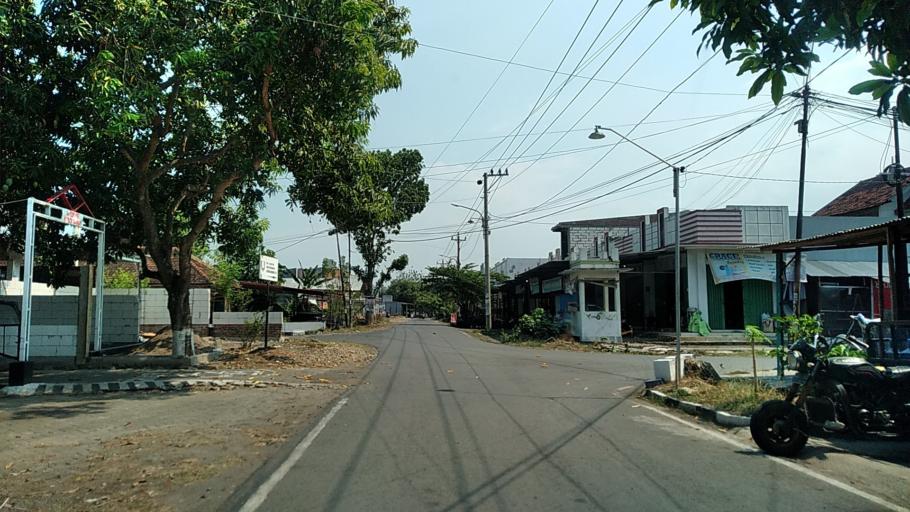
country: ID
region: Central Java
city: Mranggen
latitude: -7.0481
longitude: 110.4809
